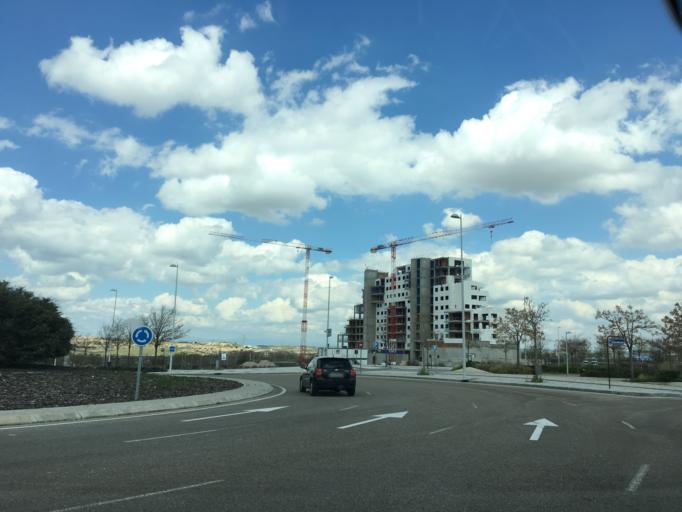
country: ES
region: Madrid
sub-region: Provincia de Madrid
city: Hortaleza
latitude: 40.4909
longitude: -3.6103
